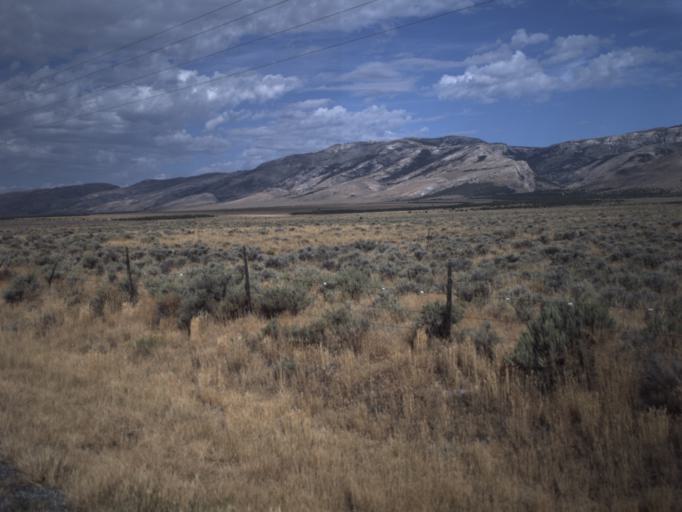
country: US
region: Idaho
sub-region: Cassia County
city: Burley
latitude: 41.8165
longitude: -113.3714
